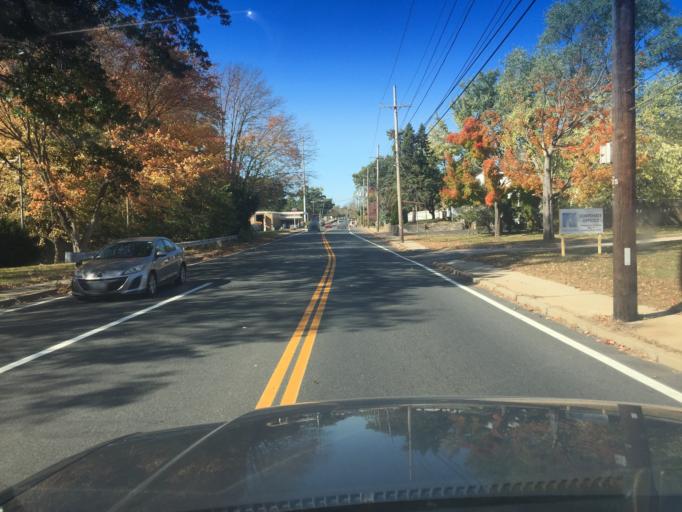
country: US
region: Rhode Island
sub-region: Providence County
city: Pawtucket
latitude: 41.8548
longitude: -71.3619
